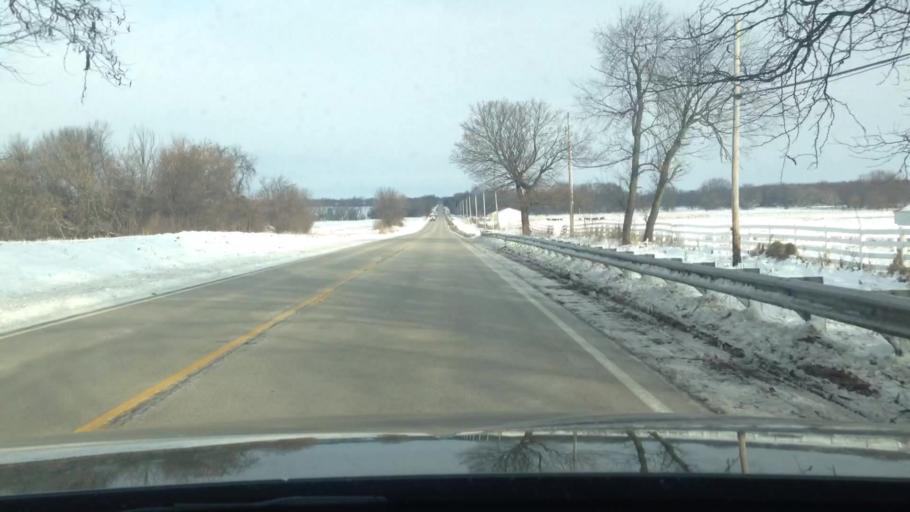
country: US
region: Illinois
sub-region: McHenry County
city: Woodstock
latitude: 42.3638
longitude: -88.4431
